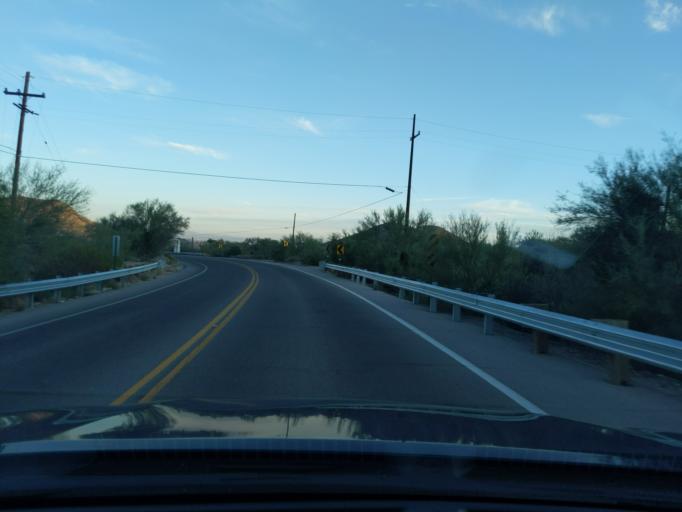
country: US
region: Arizona
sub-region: Pima County
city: Tucson Estates
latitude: 32.2256
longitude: -111.0380
